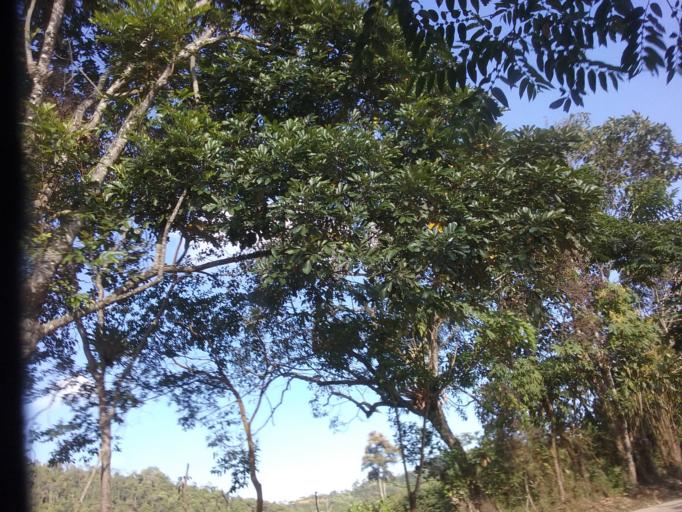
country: CO
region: Tolima
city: Libano
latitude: 4.8936
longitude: -75.0311
